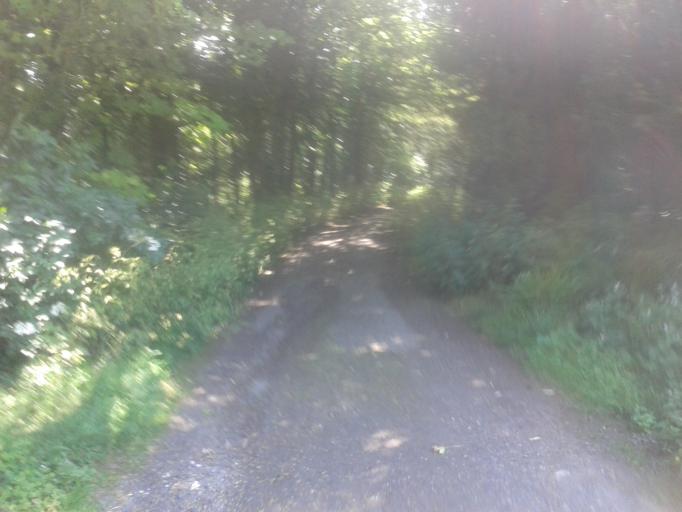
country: GB
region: England
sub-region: East Riding of Yorkshire
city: Londesborough
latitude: 53.8986
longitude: -0.6772
